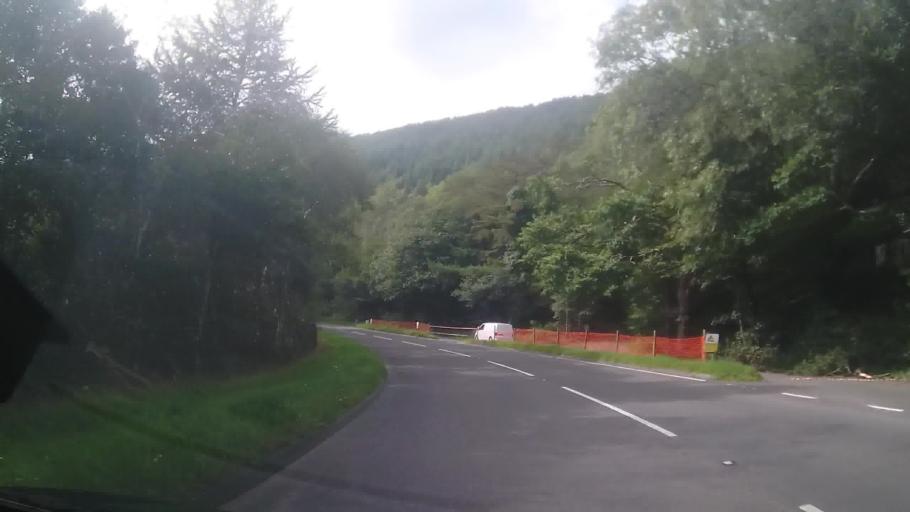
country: GB
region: Wales
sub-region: Gwynedd
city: Barmouth
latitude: 52.7481
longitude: -3.9808
